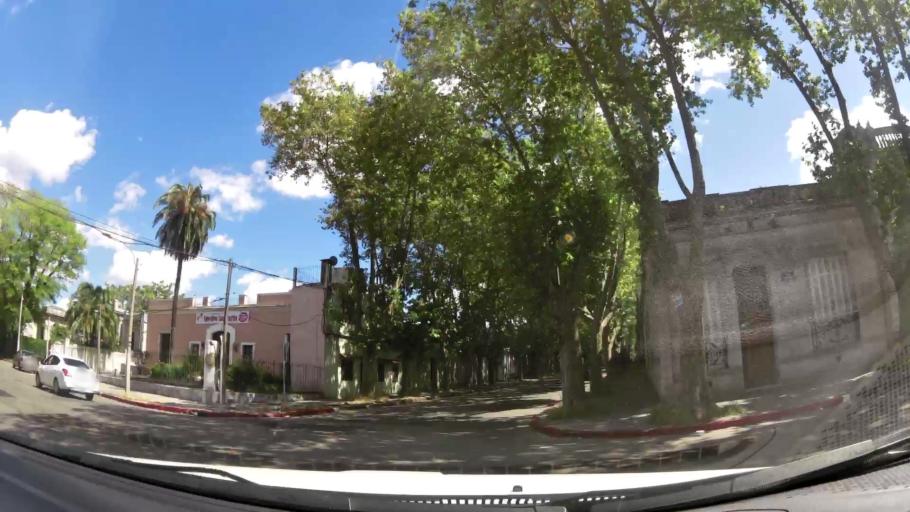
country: UY
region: Montevideo
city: Montevideo
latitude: -34.8777
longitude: -56.1931
